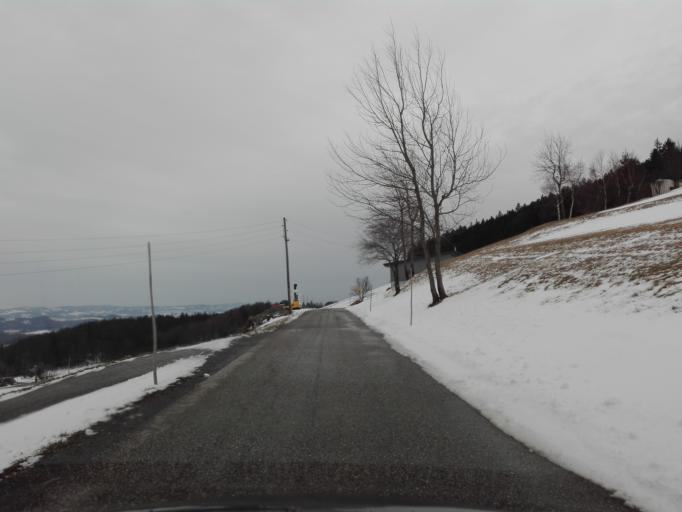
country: AT
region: Upper Austria
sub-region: Politischer Bezirk Rohrbach
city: Pfarrkirchen im Muehlkreis
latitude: 48.5601
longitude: 13.8346
